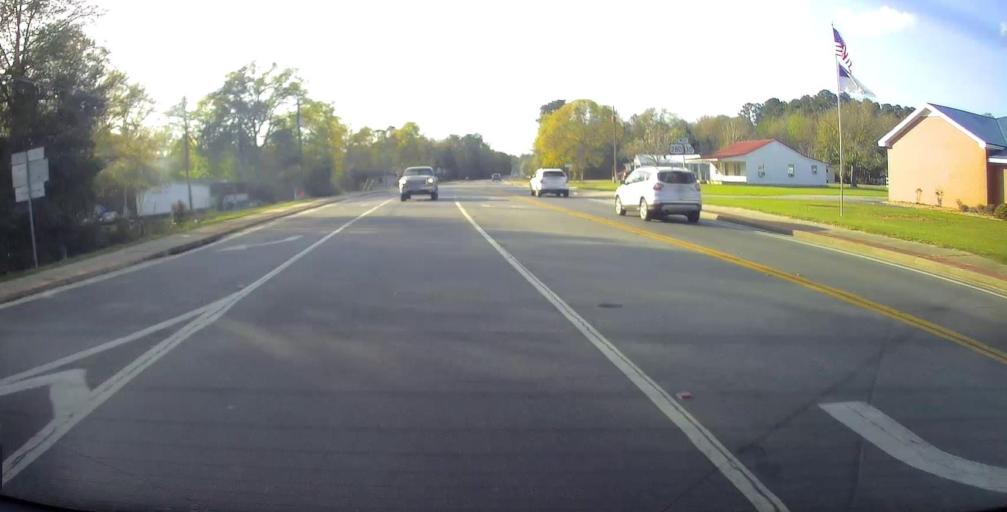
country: US
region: Georgia
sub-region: Tattnall County
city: Reidsville
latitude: 32.0814
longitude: -82.1332
